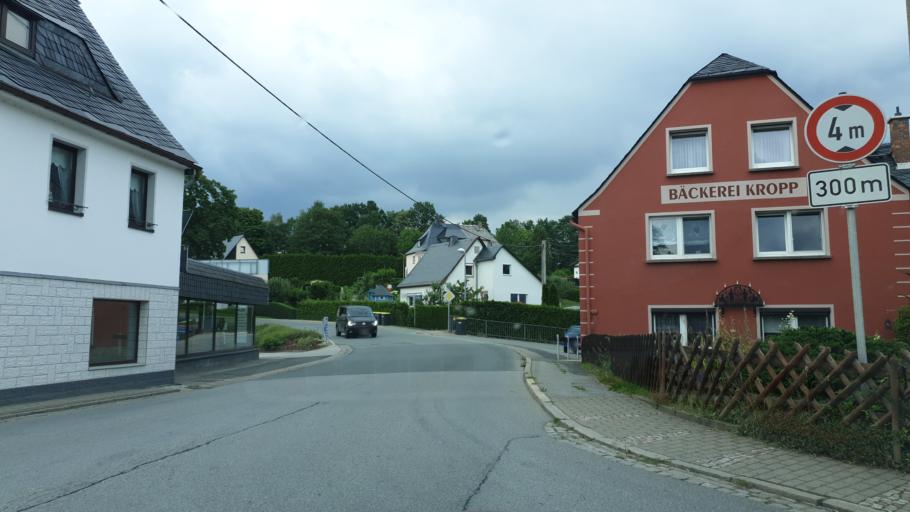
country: DE
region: Saxony
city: Zwonitz
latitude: 50.6446
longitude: 12.8223
